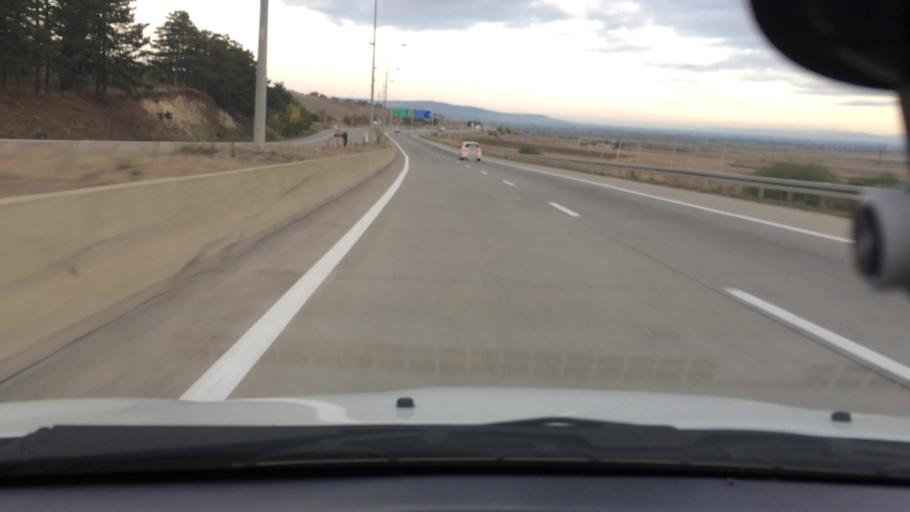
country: GE
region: Shida Kartli
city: Gori
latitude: 42.0267
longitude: 44.2048
